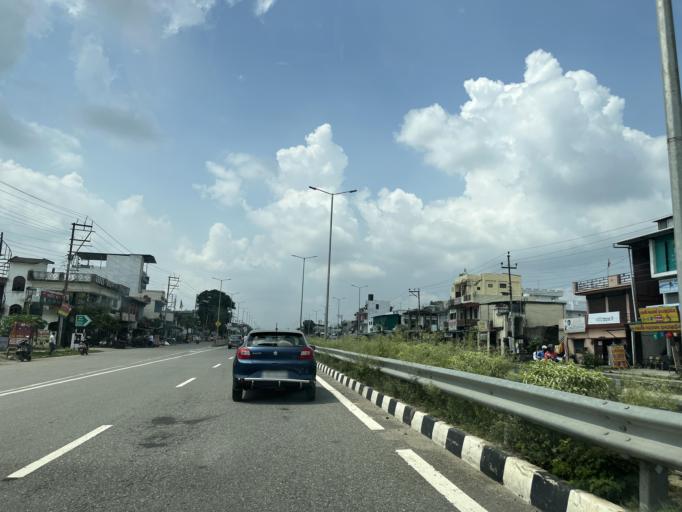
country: IN
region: Uttarakhand
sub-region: Dehradun
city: Raipur
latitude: 30.2555
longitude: 78.0927
